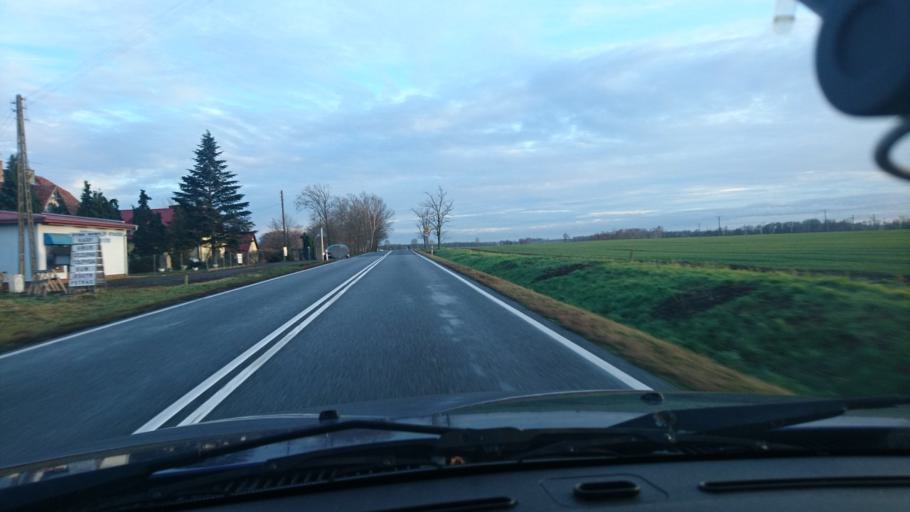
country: PL
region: Lodz Voivodeship
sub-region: Powiat wieruszowski
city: Boleslawiec
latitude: 51.1587
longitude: 18.1659
